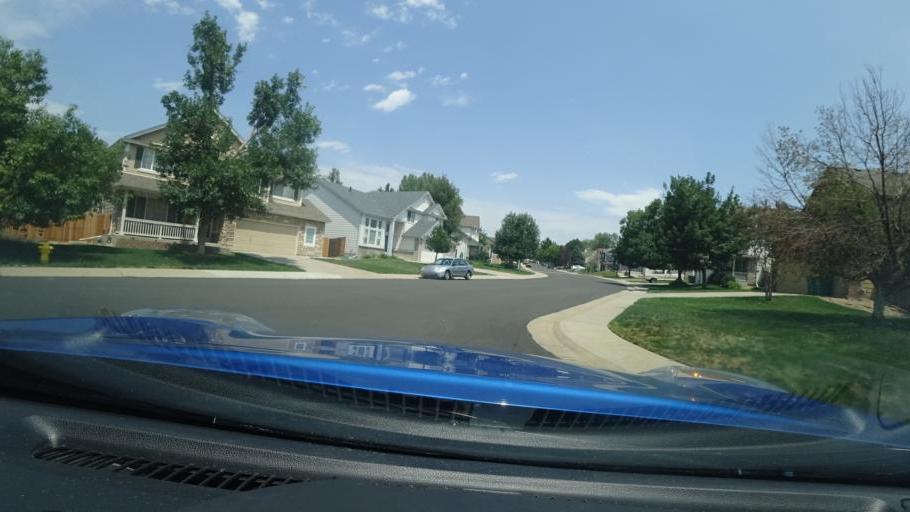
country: US
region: Colorado
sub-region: Adams County
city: Aurora
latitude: 39.6648
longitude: -104.7641
